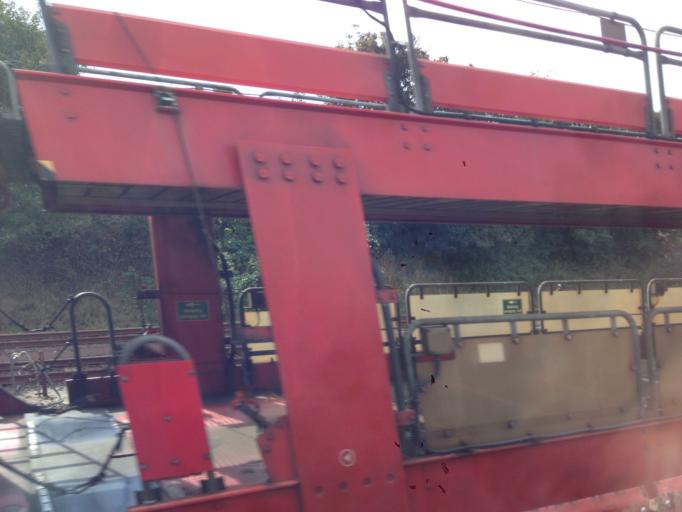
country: DE
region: Schleswig-Holstein
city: Tinnum
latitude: 54.9018
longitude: 8.3249
